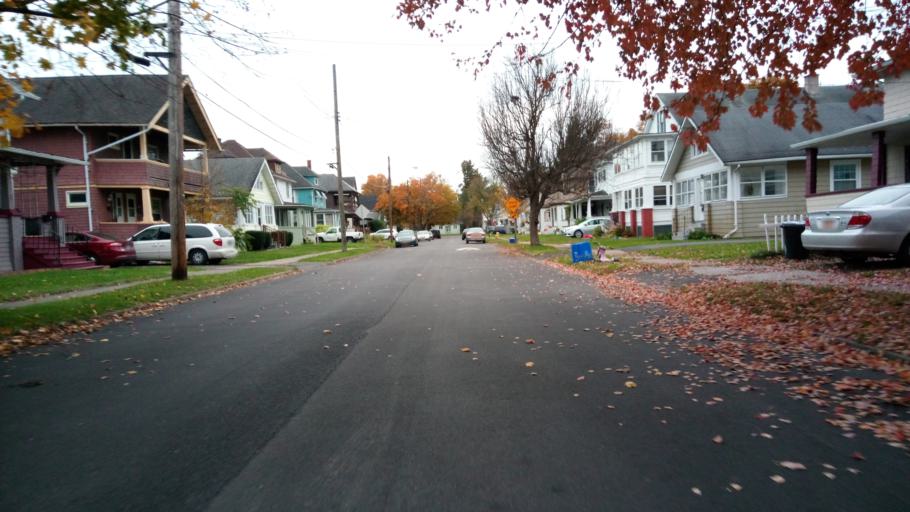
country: US
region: New York
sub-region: Chemung County
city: Elmira
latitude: 42.0836
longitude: -76.7918
